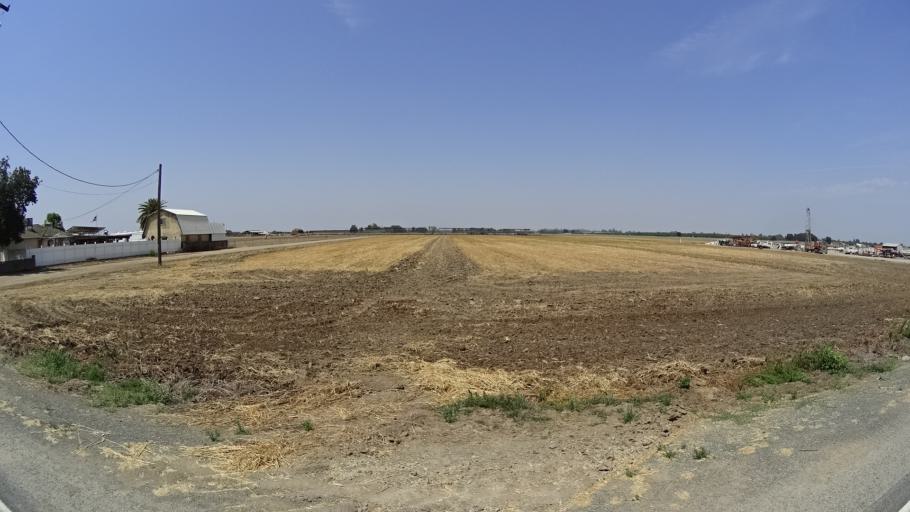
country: US
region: California
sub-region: Kings County
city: Lemoore
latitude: 36.3528
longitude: -119.7809
